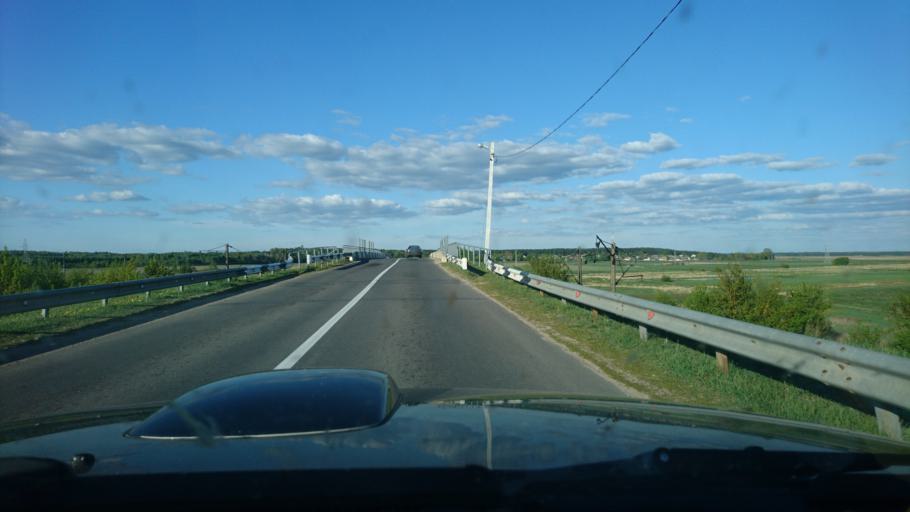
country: BY
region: Brest
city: Ivatsevichy
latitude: 52.7188
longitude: 25.3572
